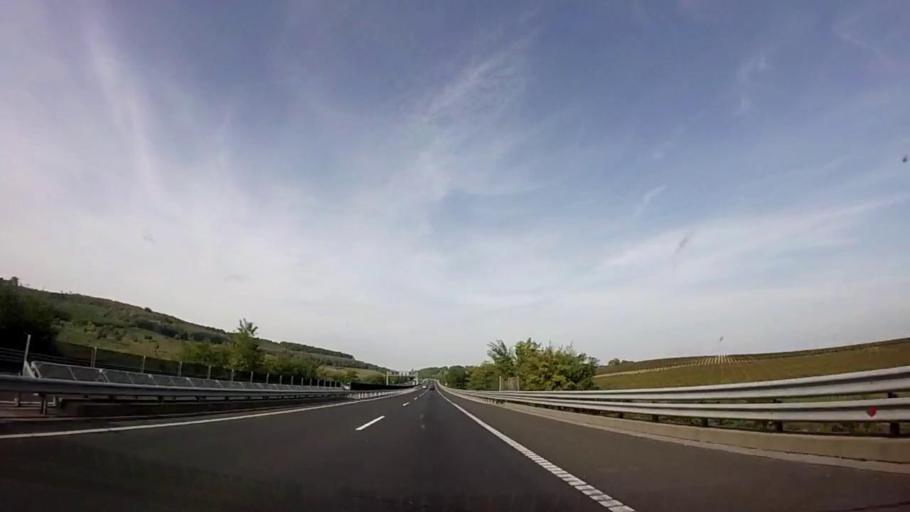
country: HU
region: Somogy
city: Balatonfoldvar
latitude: 46.8210
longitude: 17.8848
